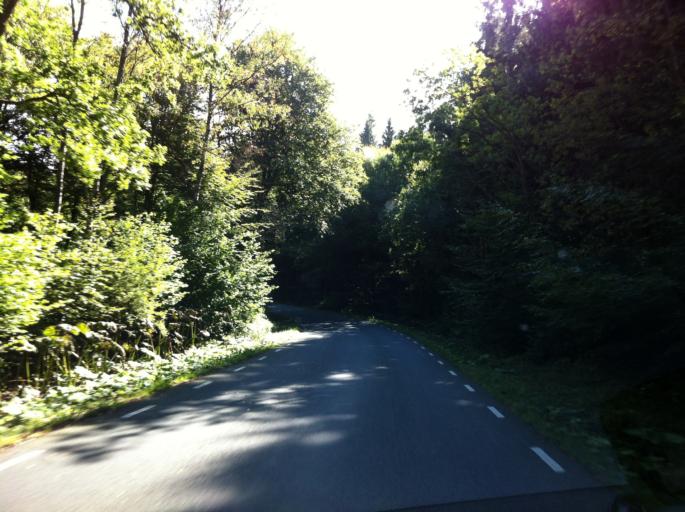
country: SE
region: Skane
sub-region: Kristianstads Kommun
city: Degeberga
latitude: 55.7515
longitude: 13.9410
